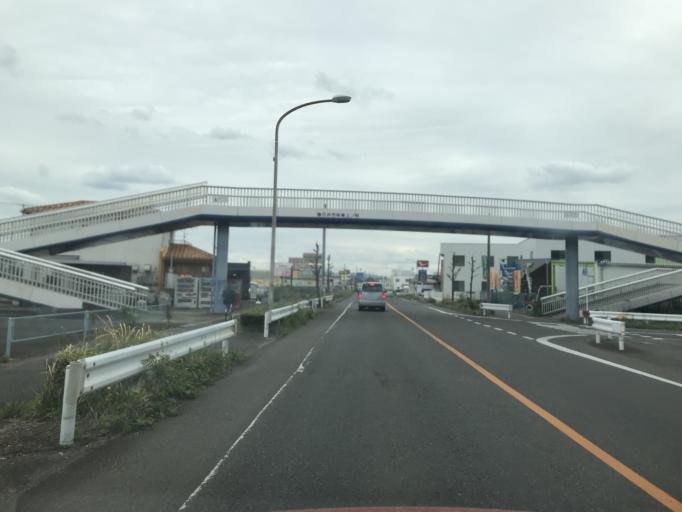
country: JP
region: Aichi
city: Kasugai
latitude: 35.2403
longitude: 136.9324
